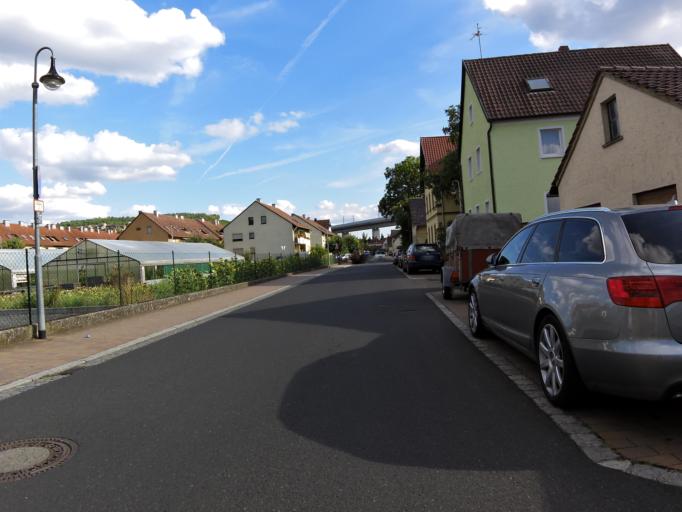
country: DE
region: Bavaria
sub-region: Regierungsbezirk Unterfranken
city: Veitshochheim
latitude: 49.8272
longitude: 9.8730
